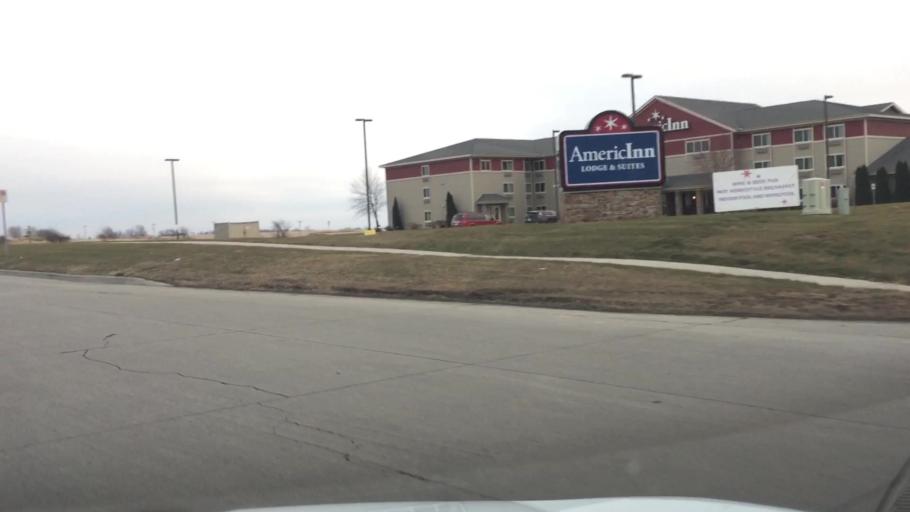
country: US
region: Iowa
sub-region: Jasper County
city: Newton
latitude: 41.6796
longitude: -92.9996
